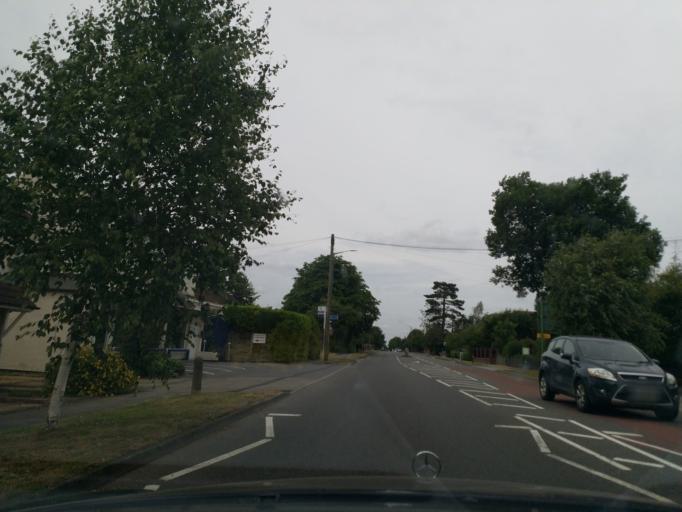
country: GB
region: England
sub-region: Solihull
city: Balsall Common
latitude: 52.3921
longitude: -1.6505
